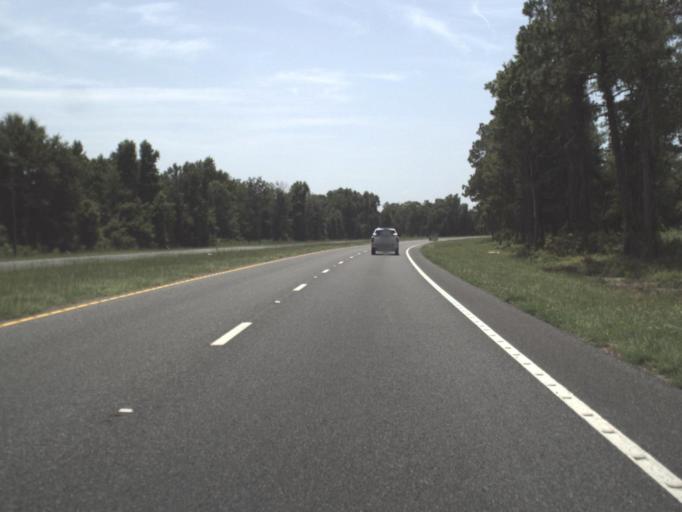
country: US
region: Florida
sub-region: Taylor County
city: Perry
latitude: 29.9481
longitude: -83.4540
